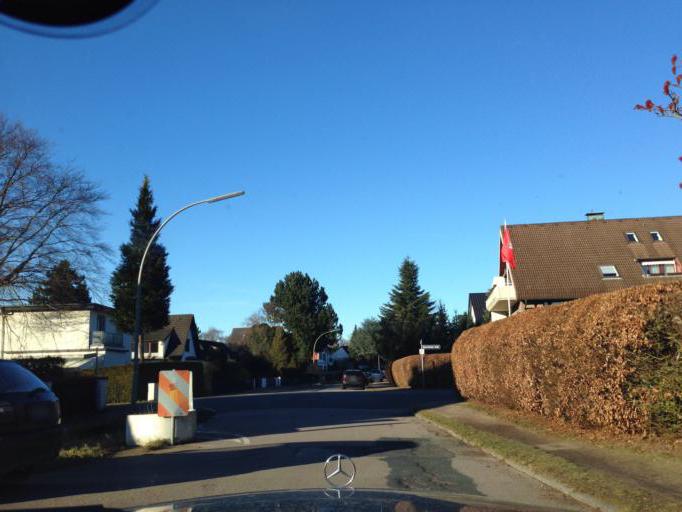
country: DE
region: Hamburg
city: Farmsen-Berne
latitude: 53.6102
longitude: 10.1281
